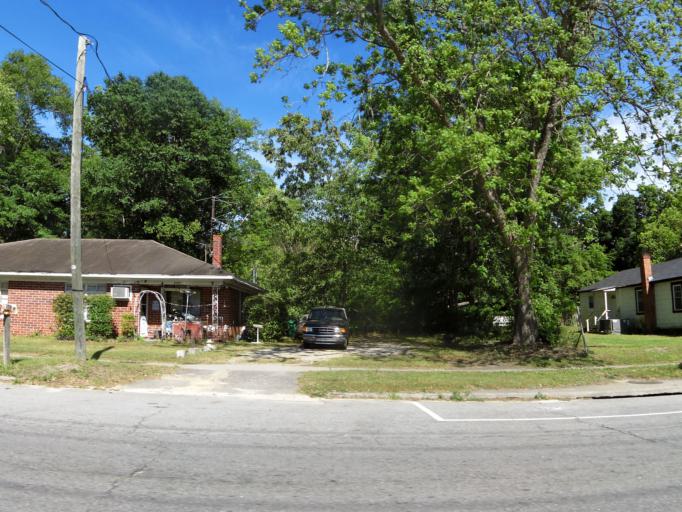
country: US
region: South Carolina
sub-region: Bamberg County
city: Denmark
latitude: 33.3201
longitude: -81.1429
